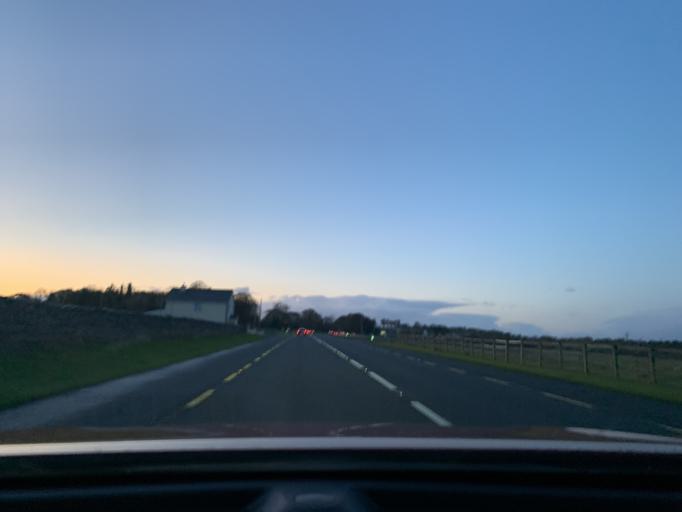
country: IE
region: Connaught
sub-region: County Leitrim
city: Carrick-on-Shannon
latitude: 53.9607
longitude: -8.1894
